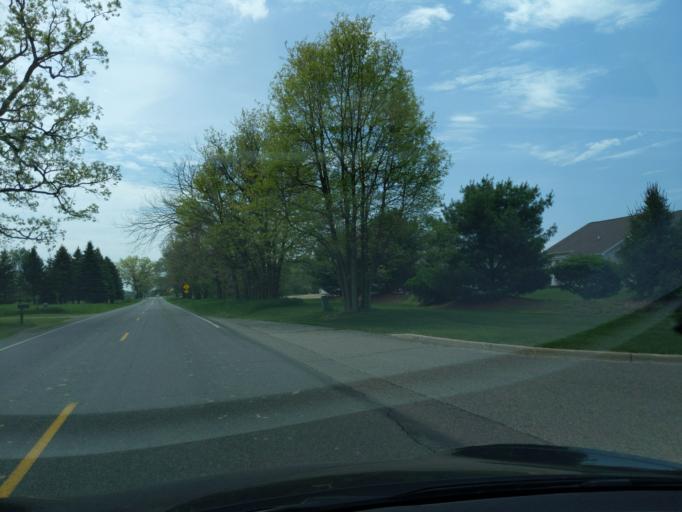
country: US
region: Michigan
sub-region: Ingham County
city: Stockbridge
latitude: 42.4574
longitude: -84.1654
